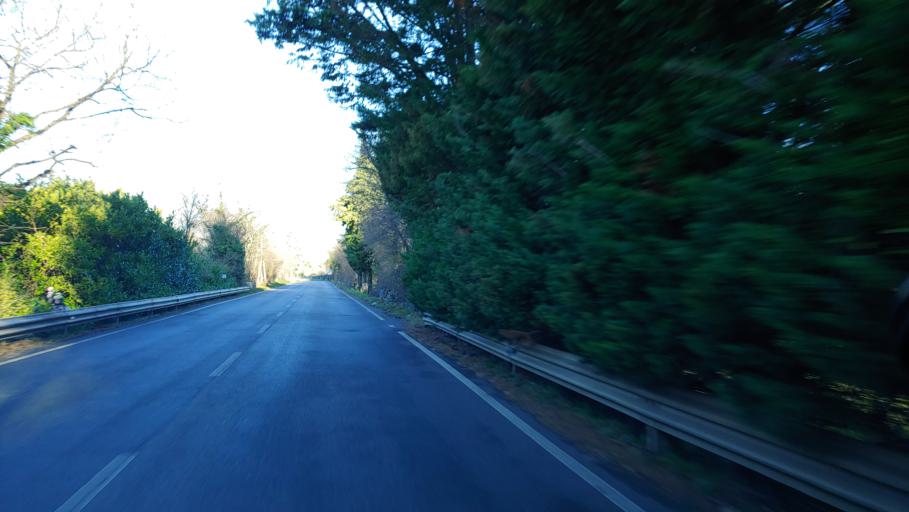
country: IT
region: Friuli Venezia Giulia
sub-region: Provincia di Trieste
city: Villa Opicina
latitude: 45.6673
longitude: 13.8304
